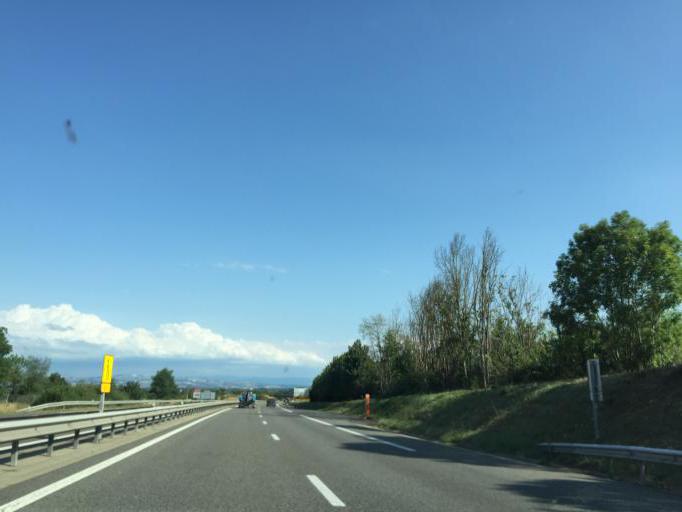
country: FR
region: Rhone-Alpes
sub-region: Departement de la Loire
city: Montrond-les-Bains
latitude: 45.6507
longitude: 4.1782
